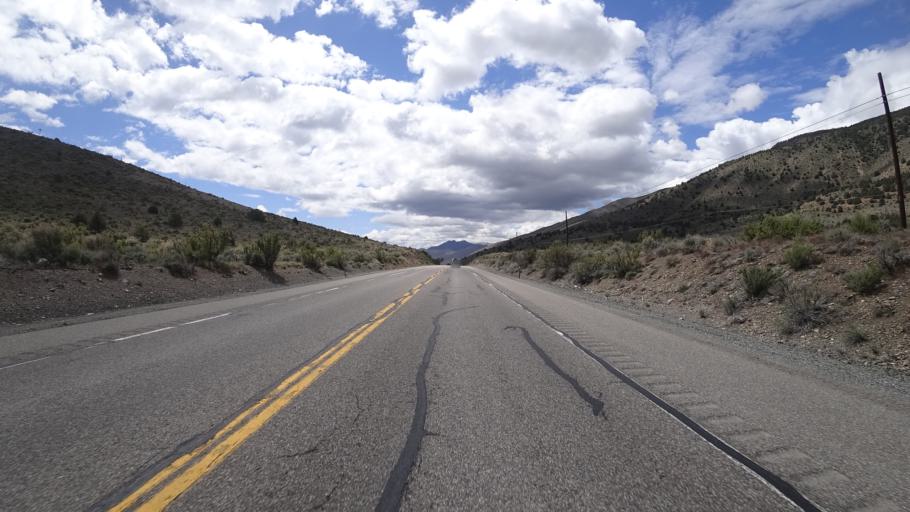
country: US
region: Nevada
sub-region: Lyon County
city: Smith Valley
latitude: 38.7133
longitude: -119.5536
